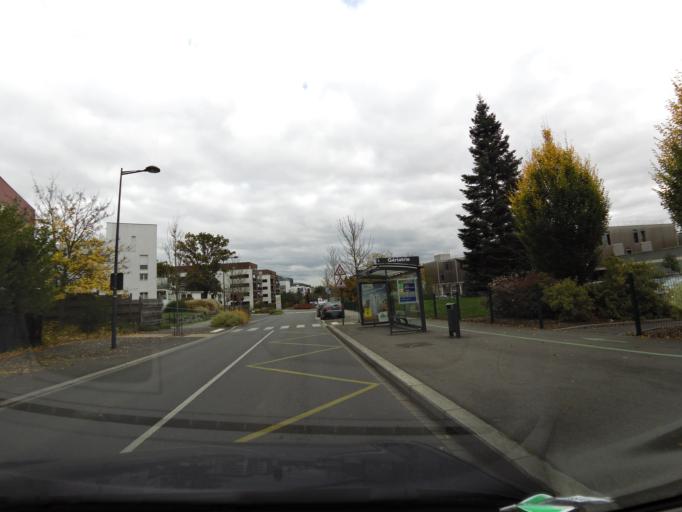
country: FR
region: Brittany
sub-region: Departement d'Ille-et-Vilaine
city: Chantepie
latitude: 48.0851
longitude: -1.6106
